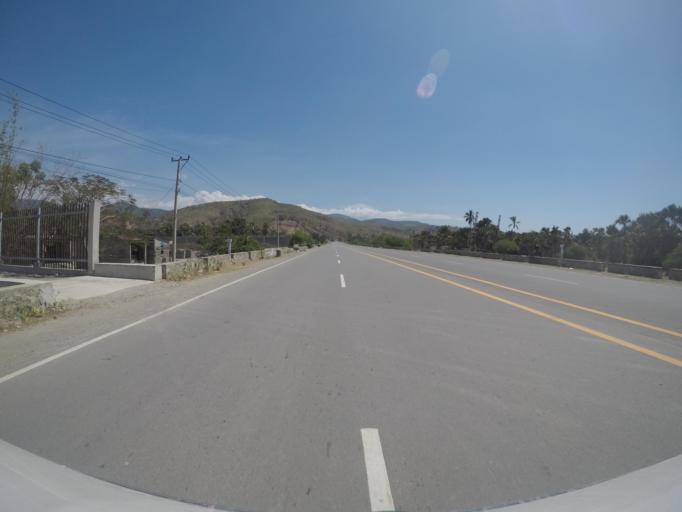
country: TL
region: Dili
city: Dili
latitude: -8.5708
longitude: 125.4870
